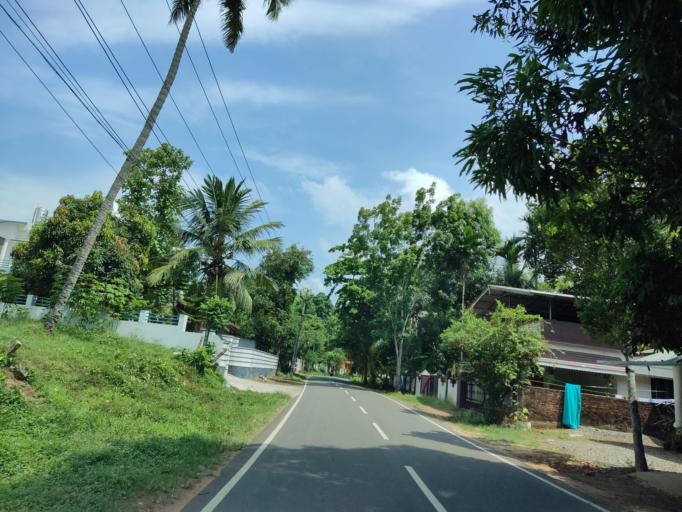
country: IN
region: Kerala
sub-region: Alappuzha
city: Mavelikara
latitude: 9.2888
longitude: 76.5711
